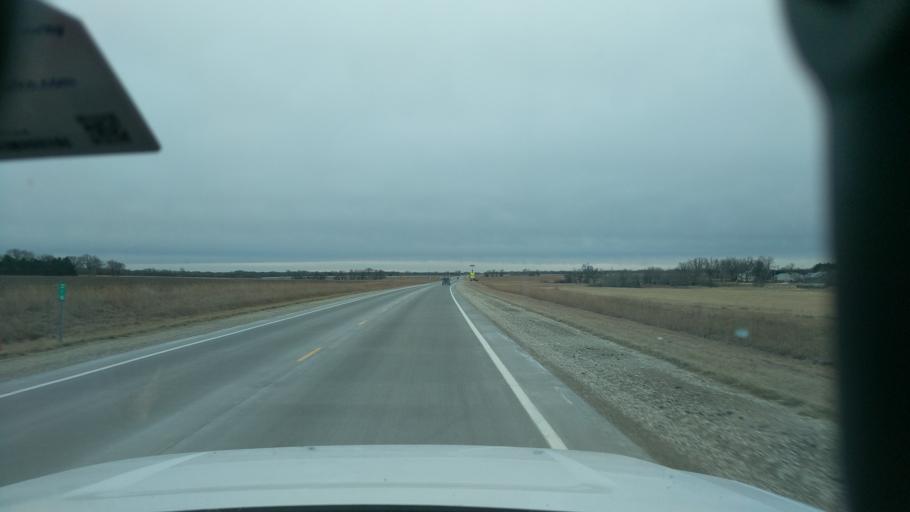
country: US
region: Kansas
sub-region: Dickinson County
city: Herington
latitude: 38.5270
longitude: -96.9562
